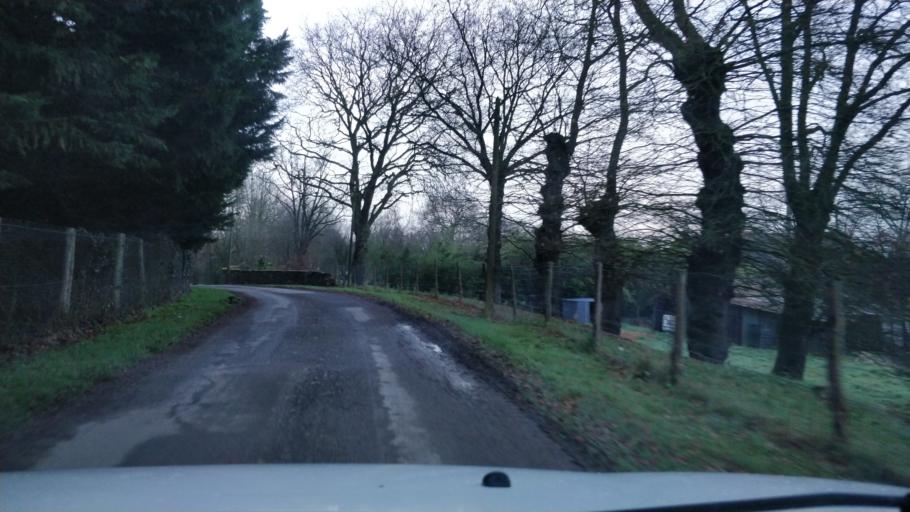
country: FR
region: Brittany
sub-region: Departement d'Ille-et-Vilaine
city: Louvigne-de-Bais
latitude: 48.0422
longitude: -1.3382
